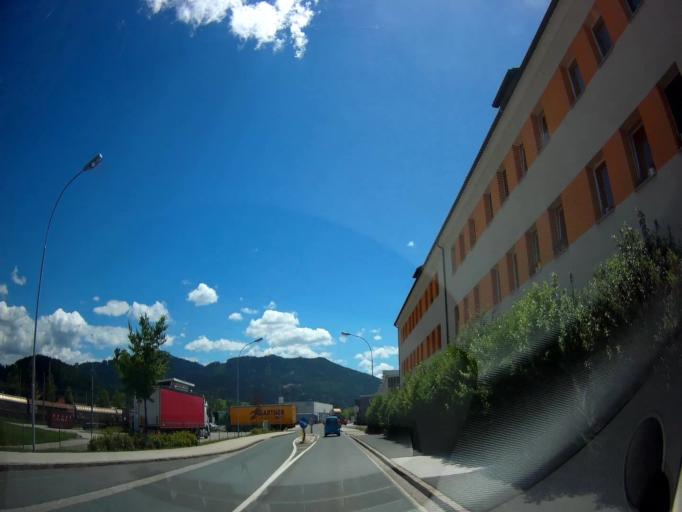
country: AT
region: Carinthia
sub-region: Politischer Bezirk Sankt Veit an der Glan
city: Sankt Veit an der Glan
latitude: 46.7553
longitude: 14.3784
